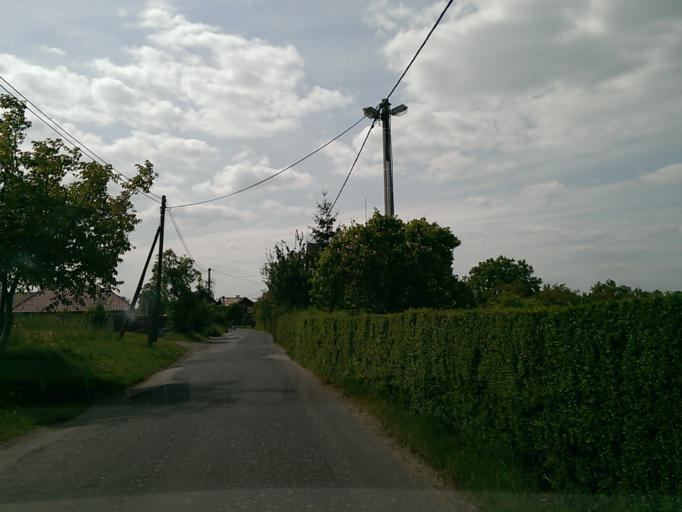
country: CZ
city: Prisovice
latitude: 50.5613
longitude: 15.0979
